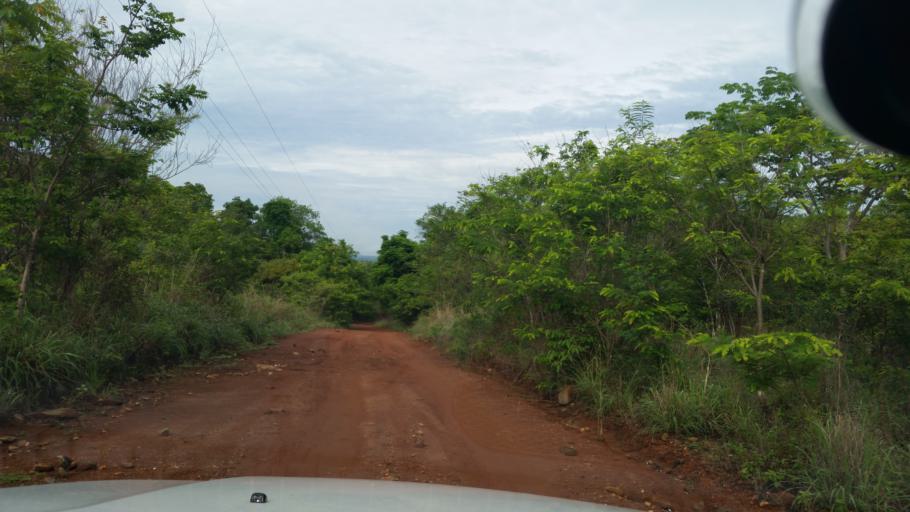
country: BR
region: Goias
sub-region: Porangatu
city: Porangatu
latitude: -13.9802
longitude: -49.2713
